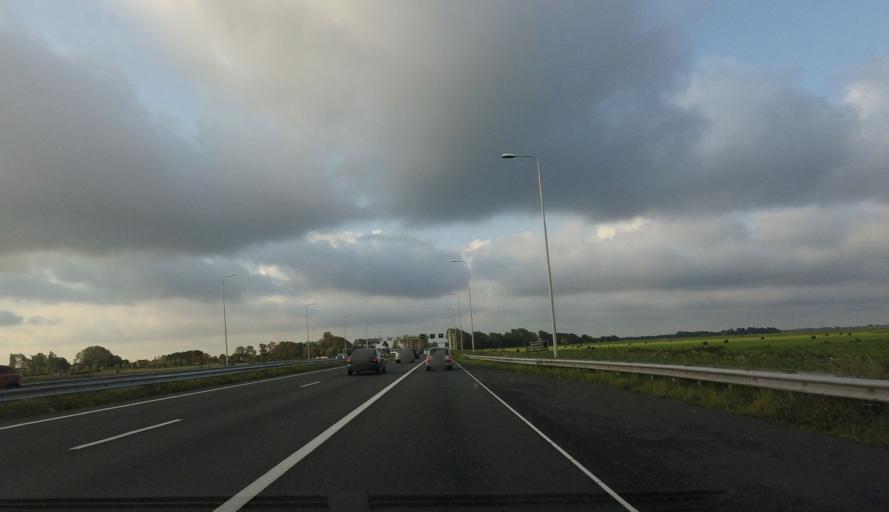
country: NL
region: North Holland
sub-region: Gemeente Uitgeest
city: Uitgeest
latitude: 52.5579
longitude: 4.7180
